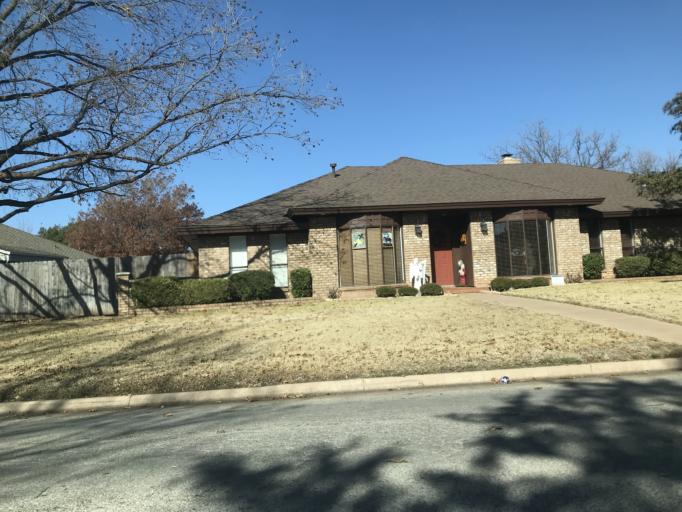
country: US
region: Texas
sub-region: Taylor County
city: Abilene
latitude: 32.3828
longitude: -99.7640
